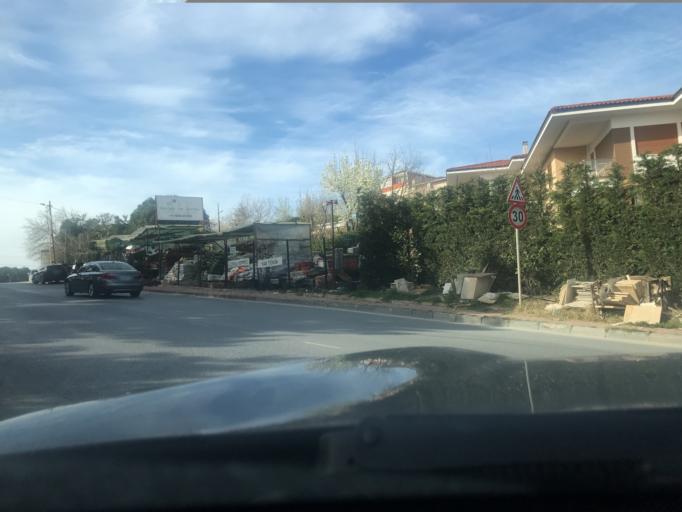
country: TR
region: Istanbul
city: Umraniye
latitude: 41.0510
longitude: 29.1729
